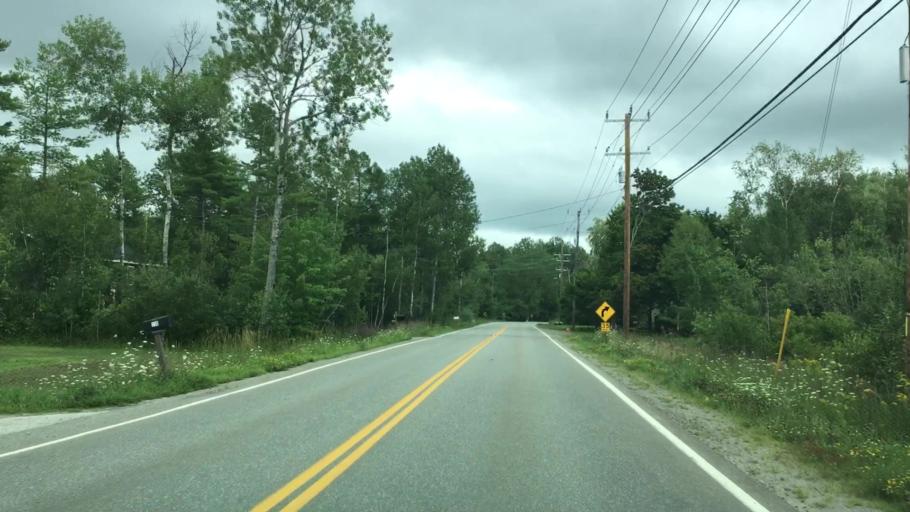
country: US
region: Maine
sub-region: Penobscot County
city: Brewer
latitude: 44.7675
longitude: -68.7587
